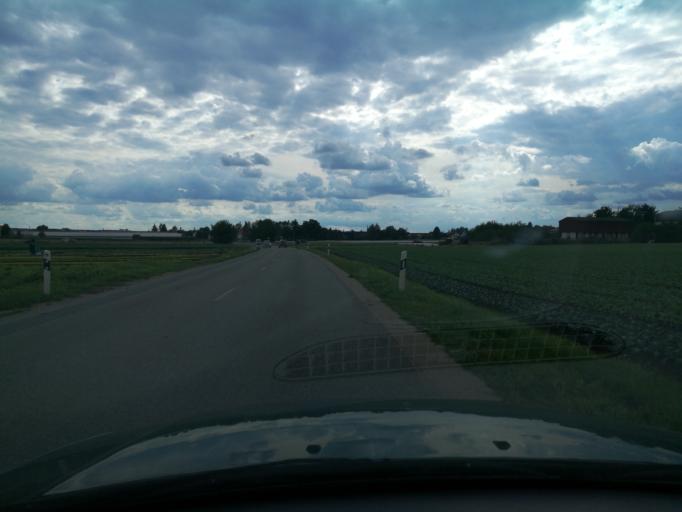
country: DE
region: Bavaria
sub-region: Regierungsbezirk Mittelfranken
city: Wetzendorf
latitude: 49.4874
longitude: 11.0198
